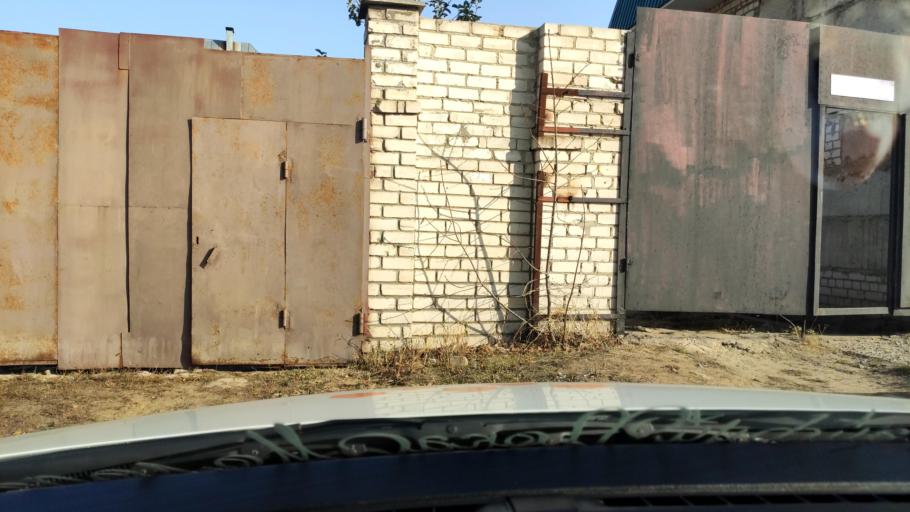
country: RU
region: Voronezj
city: Pridonskoy
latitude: 51.6555
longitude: 39.0948
